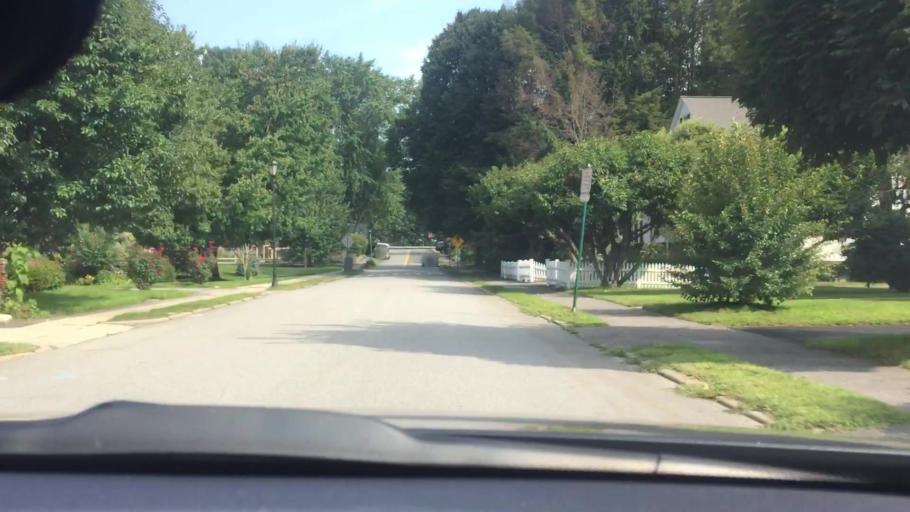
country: US
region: Massachusetts
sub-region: Norfolk County
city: Wellesley
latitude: 42.3052
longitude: -71.2802
